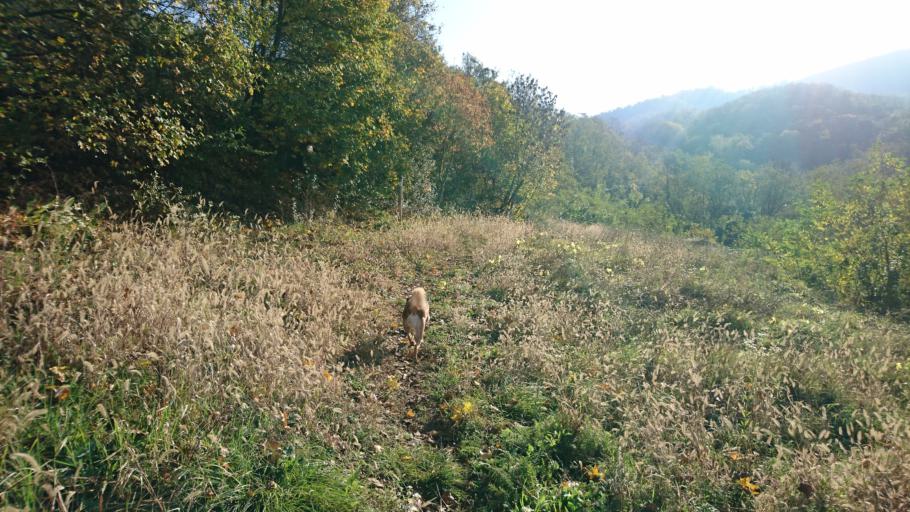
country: IT
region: Veneto
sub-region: Provincia di Padova
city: Fontanafredda
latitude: 45.3240
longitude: 11.6840
